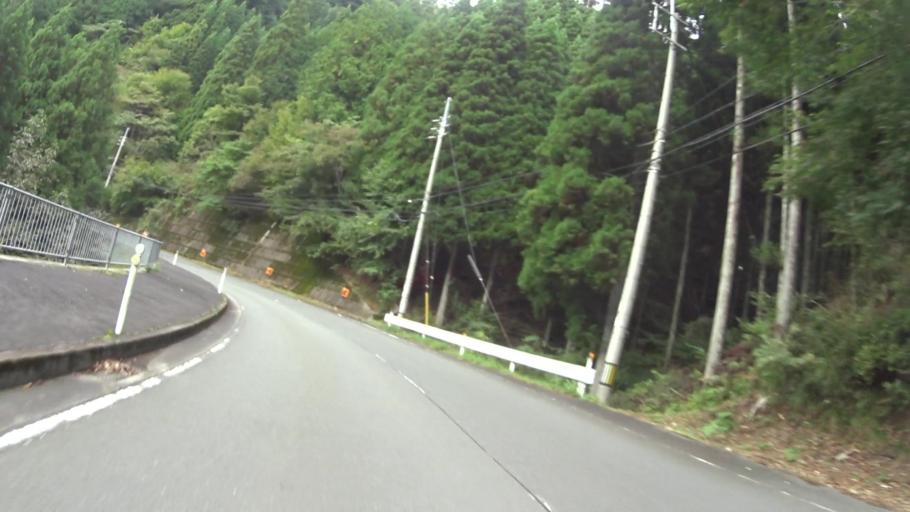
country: JP
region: Fukui
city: Obama
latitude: 35.3157
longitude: 135.6493
